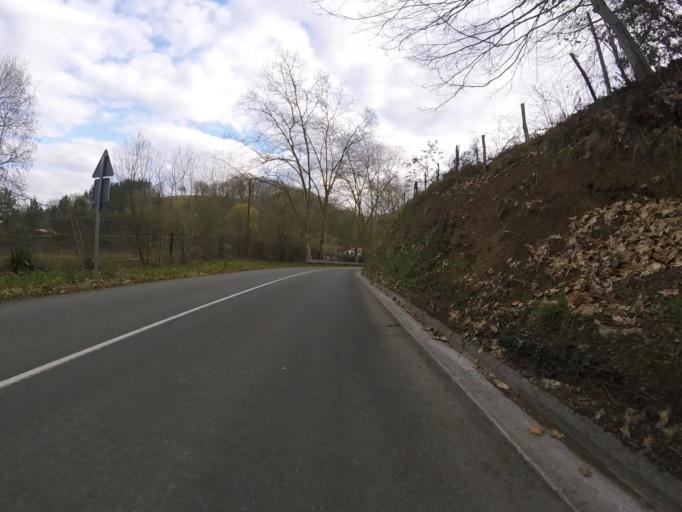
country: ES
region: Basque Country
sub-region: Provincia de Guipuzcoa
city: Irun
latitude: 43.3176
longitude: -1.8191
